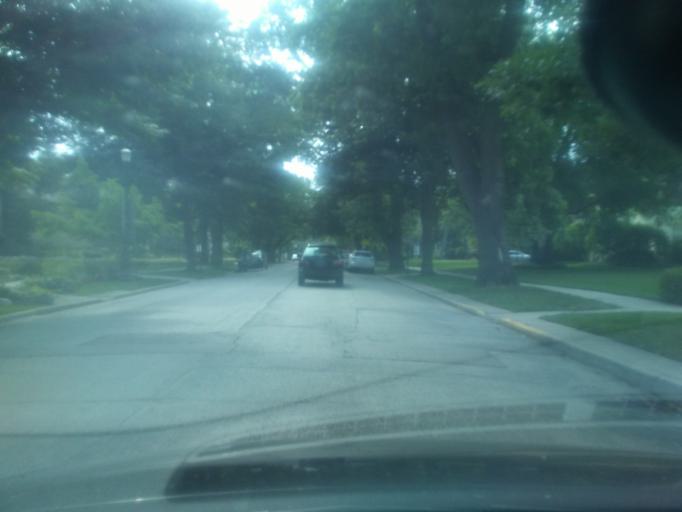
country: US
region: Illinois
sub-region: Cook County
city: Evanston
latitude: 42.0622
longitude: -87.6942
